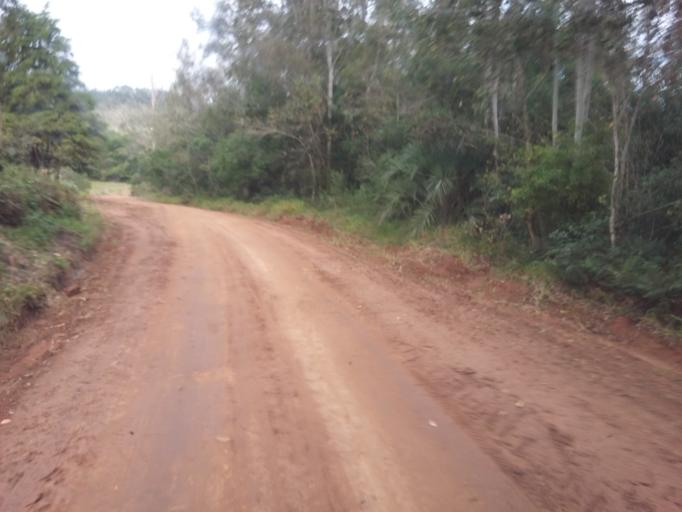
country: BR
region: Rio Grande do Sul
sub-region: Camaqua
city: Camaqua
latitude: -30.7112
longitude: -51.7801
